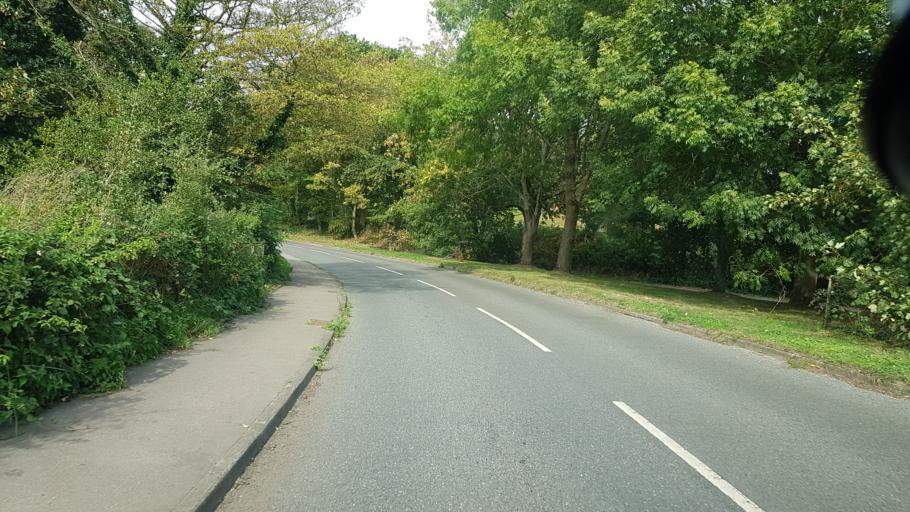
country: GB
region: England
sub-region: Kent
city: West Malling
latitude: 51.3039
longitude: 0.3809
